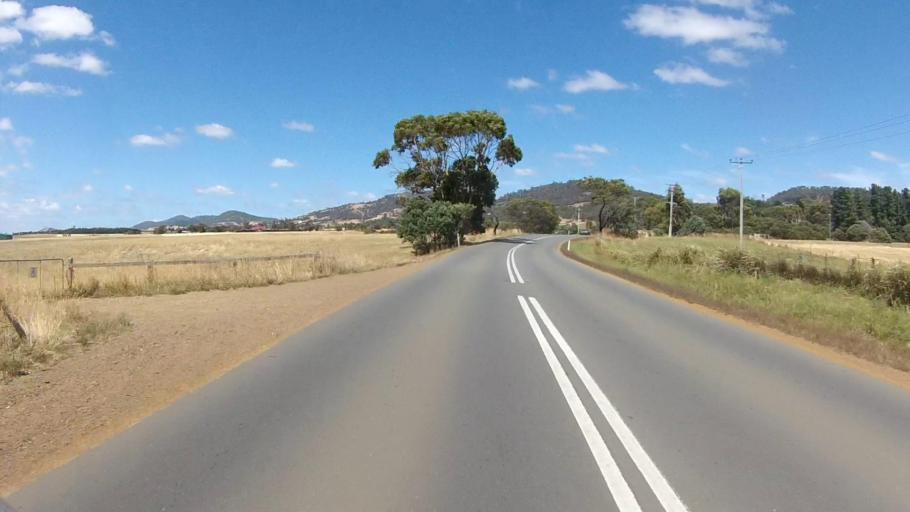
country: AU
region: Tasmania
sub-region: Clarence
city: Cambridge
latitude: -42.7703
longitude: 147.4161
